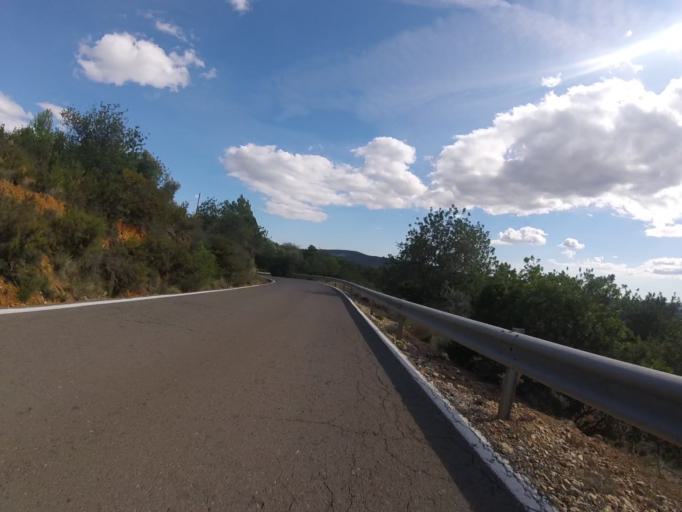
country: ES
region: Valencia
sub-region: Provincia de Castello
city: Cuevas de Vinroma
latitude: 40.3755
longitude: 0.1133
